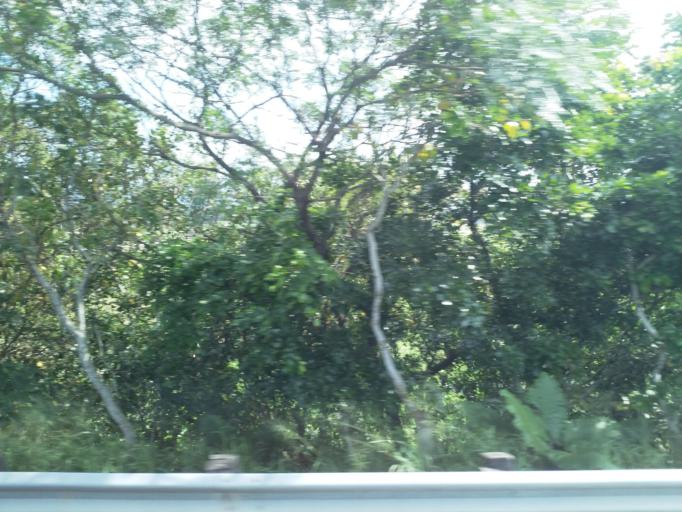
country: TW
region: Taiwan
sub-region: Pingtung
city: Pingtung
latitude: 22.8594
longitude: 120.4926
